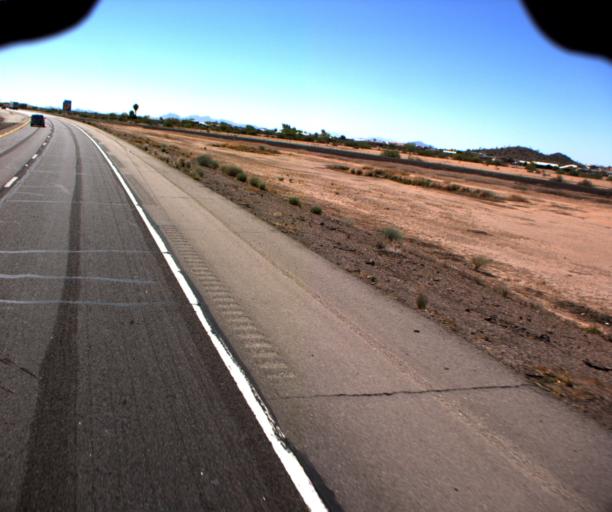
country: US
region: Arizona
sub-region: Pinal County
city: Arizona City
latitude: 32.8177
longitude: -111.6826
